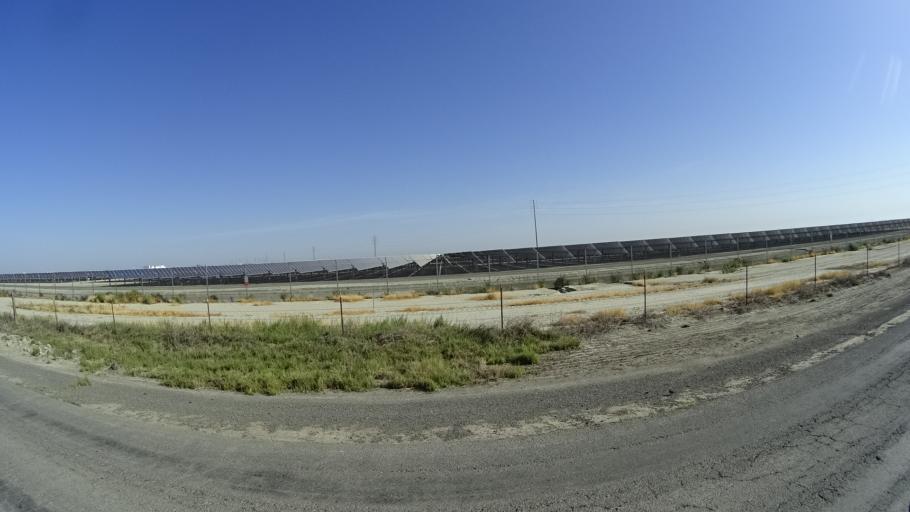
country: US
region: California
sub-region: Kings County
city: Corcoran
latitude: 36.1379
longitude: -119.5793
